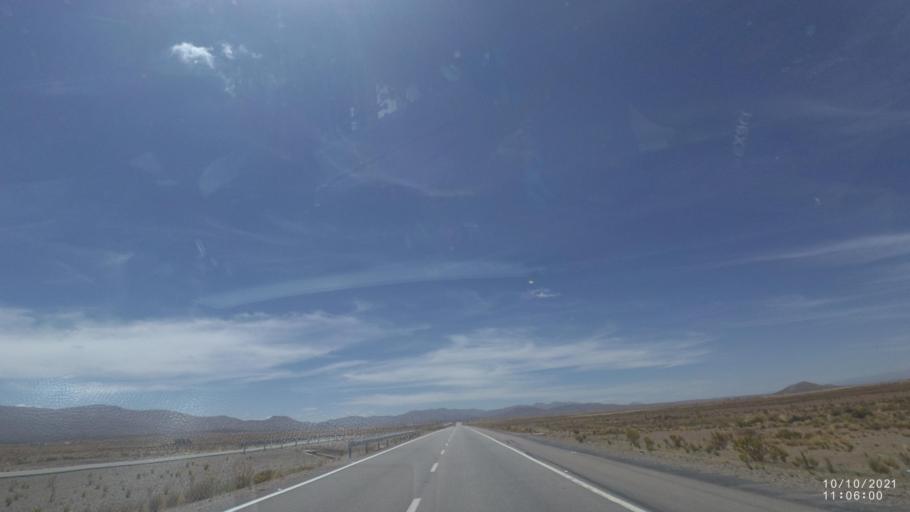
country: BO
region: La Paz
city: Colquiri
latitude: -17.6579
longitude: -67.0953
